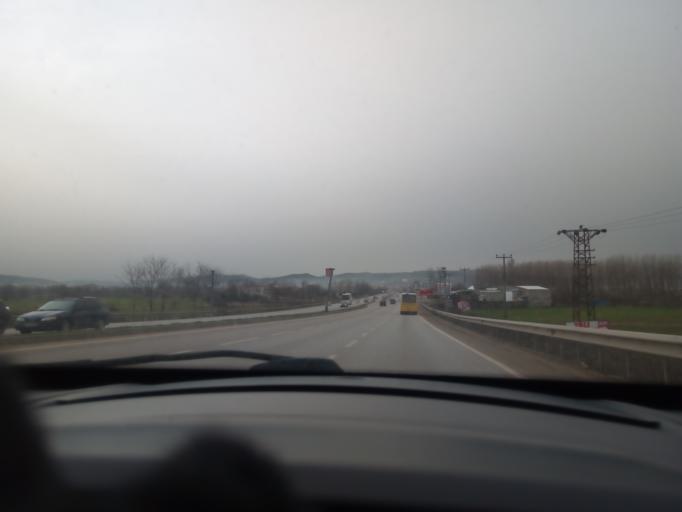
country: TR
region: Balikesir
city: Susurluk
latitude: 39.9425
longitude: 28.1654
